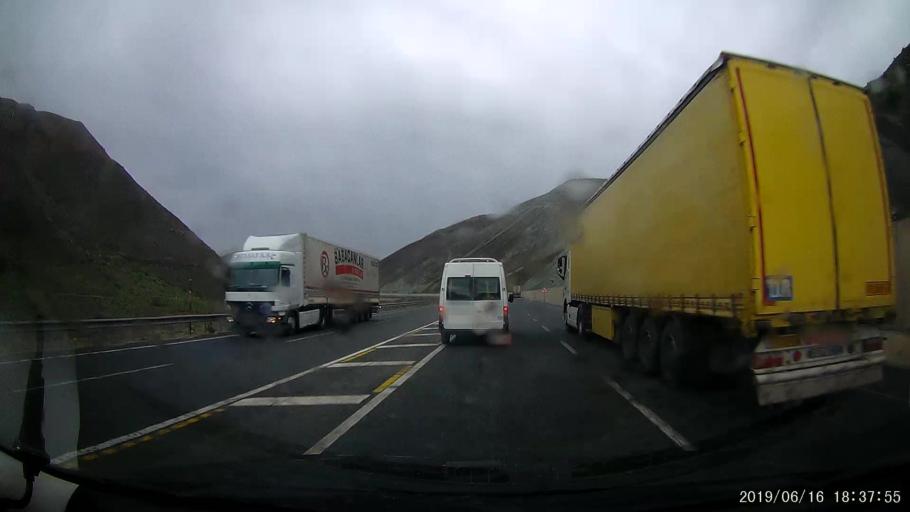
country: TR
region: Erzincan
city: Catalarmut
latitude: 39.8848
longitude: 39.1902
